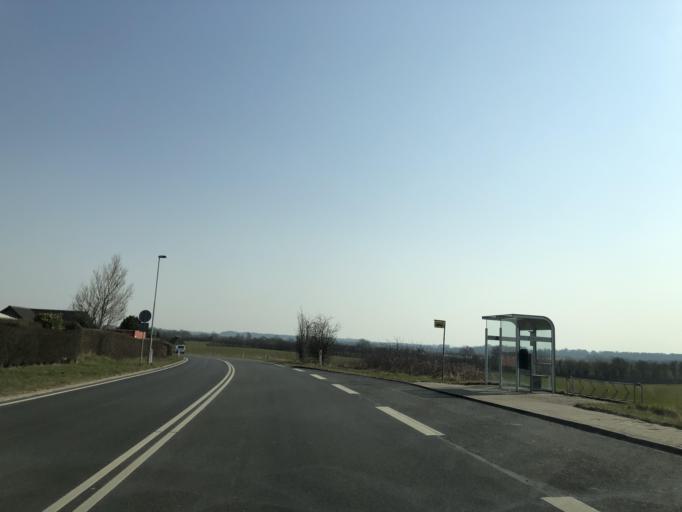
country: DK
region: South Denmark
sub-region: Sonderborg Kommune
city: Nordborg
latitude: 55.0341
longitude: 9.7528
